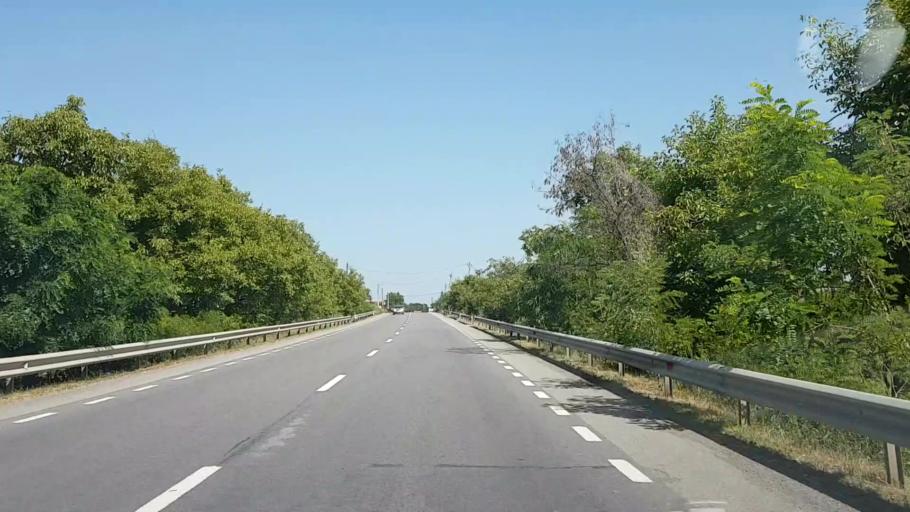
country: RO
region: Bistrita-Nasaud
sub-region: Comuna Uriu
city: Cristestii Ciceului
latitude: 47.1834
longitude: 24.1306
